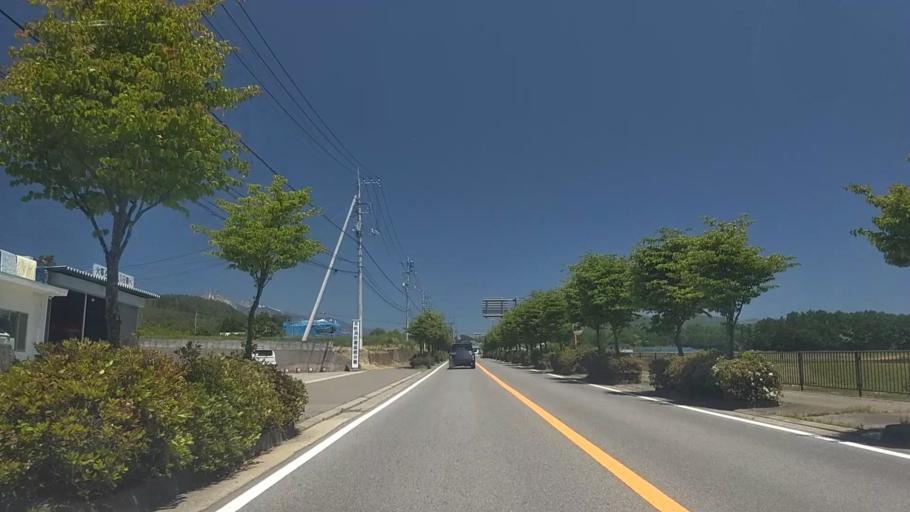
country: JP
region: Yamanashi
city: Nirasaki
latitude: 35.8414
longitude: 138.4332
